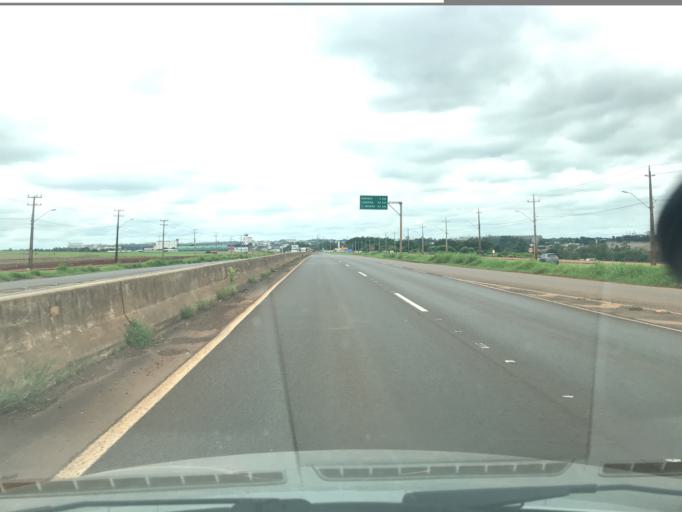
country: BR
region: Parana
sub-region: Paicandu
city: Paicandu
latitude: -23.4566
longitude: -52.0200
